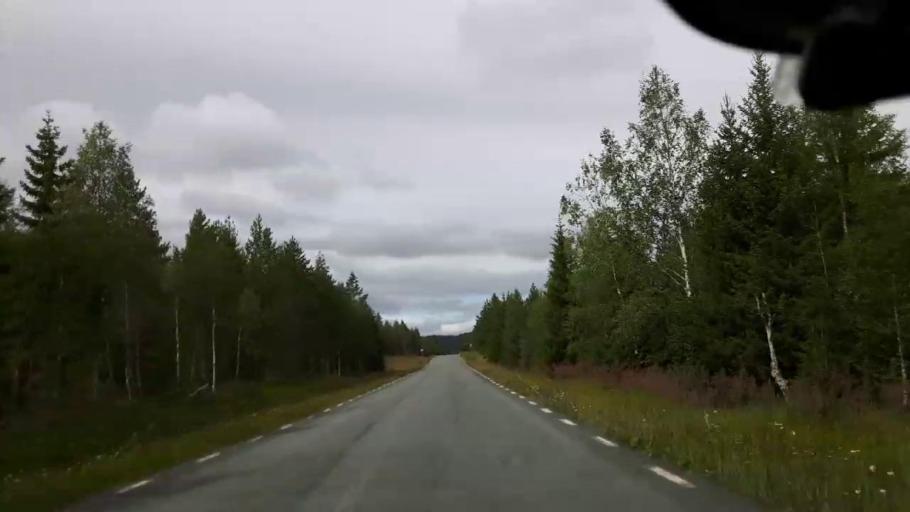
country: SE
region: Jaemtland
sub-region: Krokoms Kommun
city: Valla
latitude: 63.4752
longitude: 13.9966
